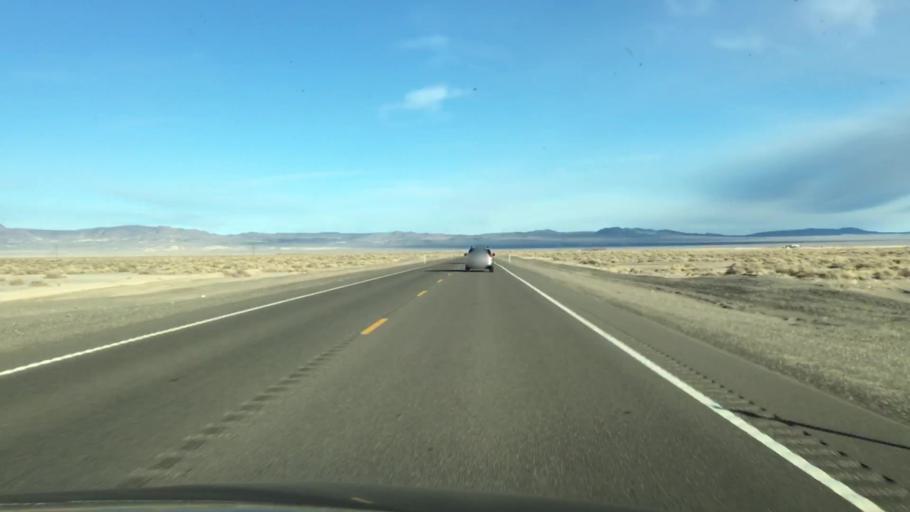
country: US
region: Nevada
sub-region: Nye County
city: Tonopah
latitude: 38.1384
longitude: -117.4989
